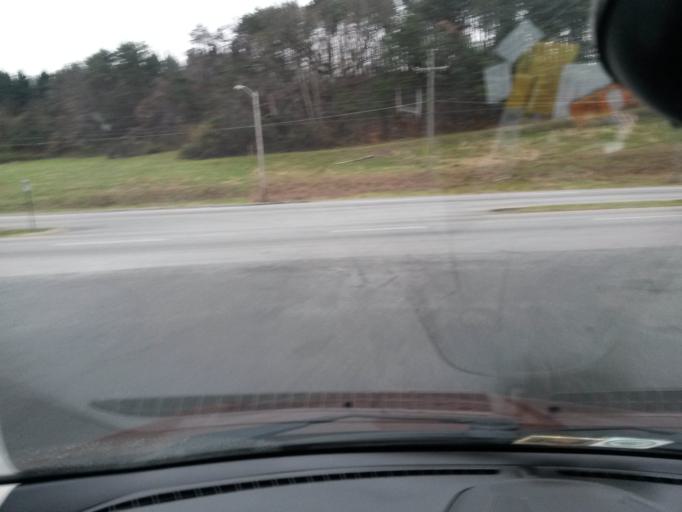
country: US
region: Virginia
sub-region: Roanoke County
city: Vinton
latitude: 37.2989
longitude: -79.8965
